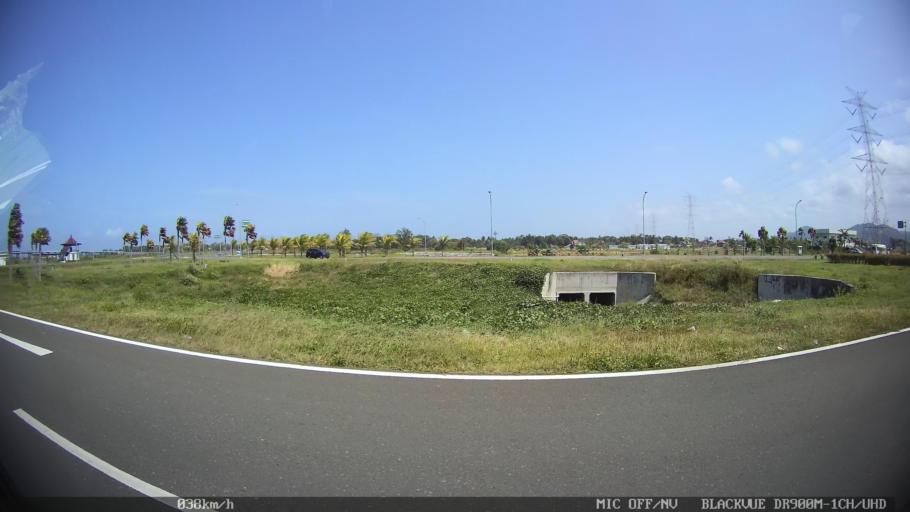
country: ID
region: Daerah Istimewa Yogyakarta
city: Srandakan
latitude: -7.8908
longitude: 110.0625
